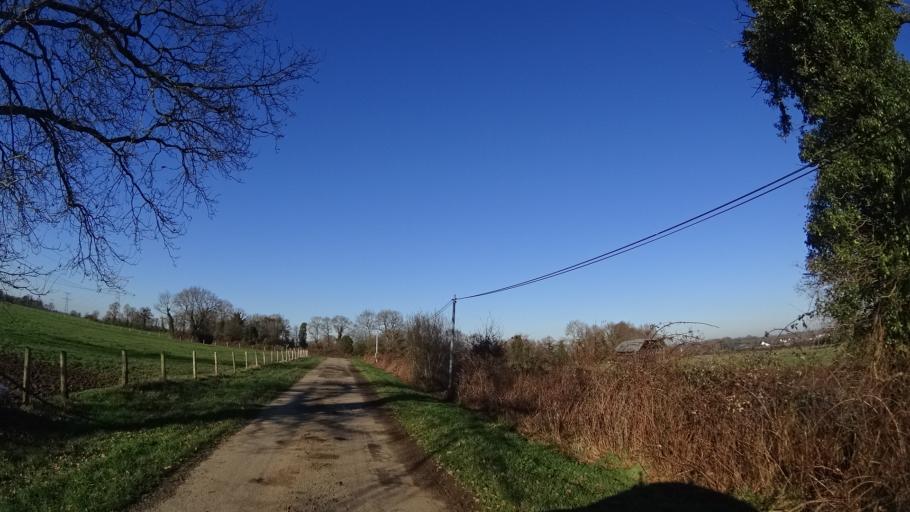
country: FR
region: Brittany
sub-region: Departement du Morbihan
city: Allaire
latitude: 47.6293
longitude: -2.1817
